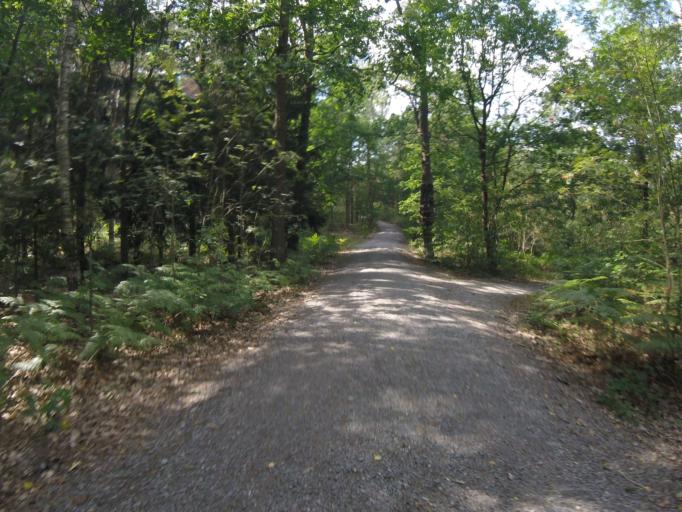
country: DE
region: Brandenburg
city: Munchehofe
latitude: 52.0600
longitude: 13.7916
